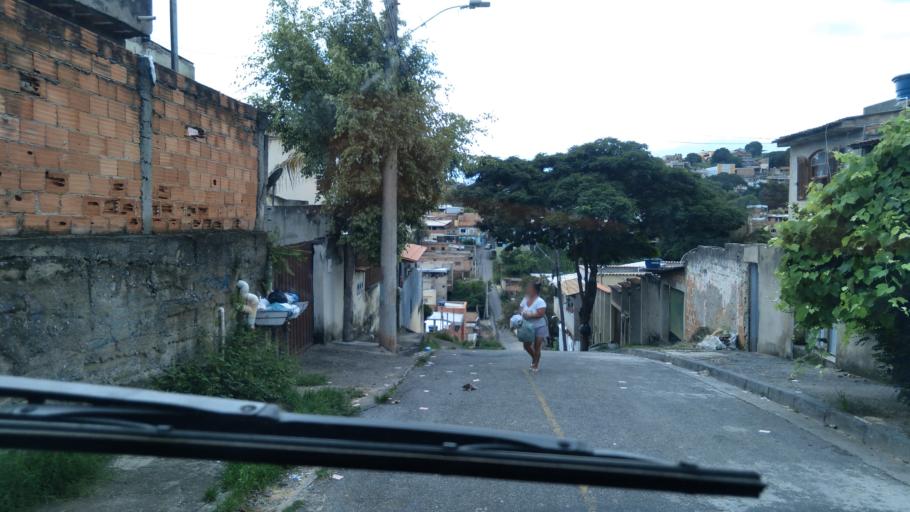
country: BR
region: Minas Gerais
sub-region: Santa Luzia
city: Santa Luzia
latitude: -19.8338
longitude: -43.8964
